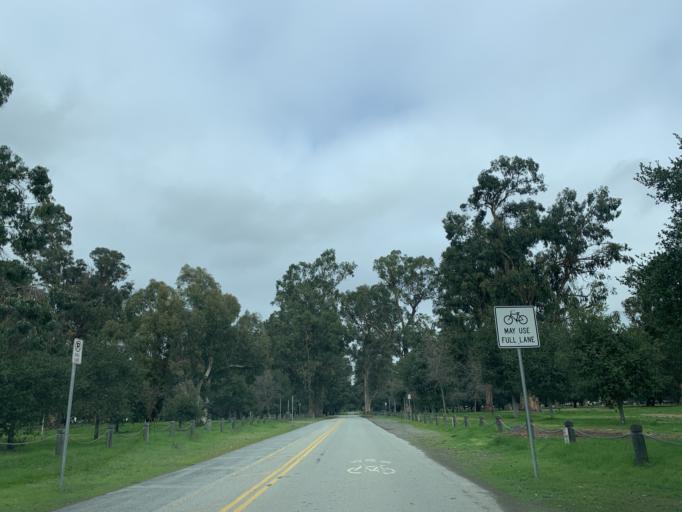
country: US
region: California
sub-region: Santa Clara County
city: Stanford
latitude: 37.4356
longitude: -122.1658
